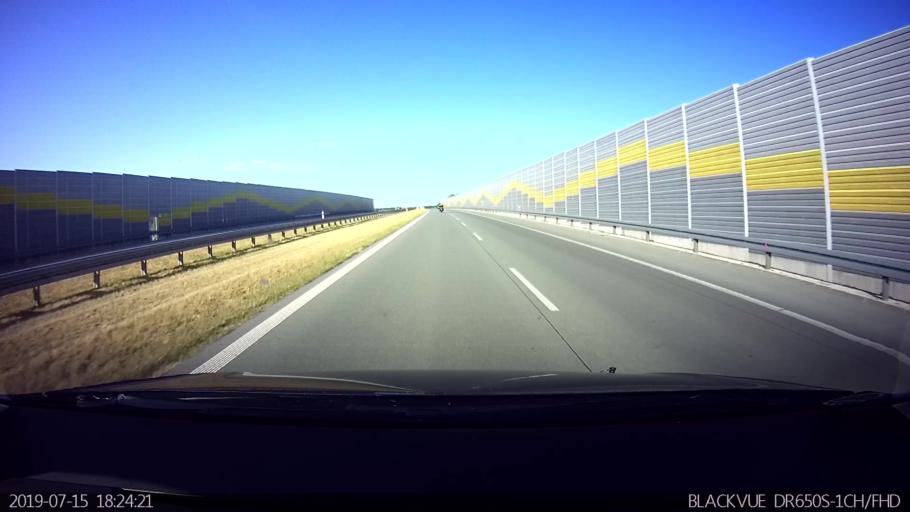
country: PL
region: Lodz Voivodeship
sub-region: Powiat laski
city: Lask
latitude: 51.5656
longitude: 19.1559
